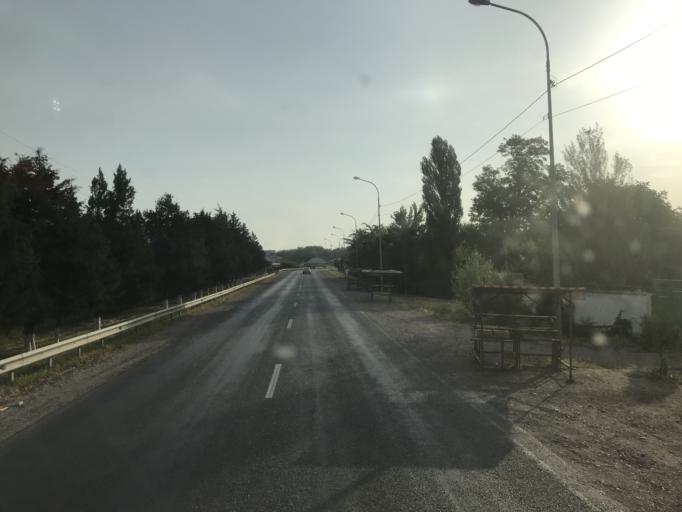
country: KZ
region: Ongtustik Qazaqstan
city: Saryaghash
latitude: 41.4878
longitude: 69.2579
